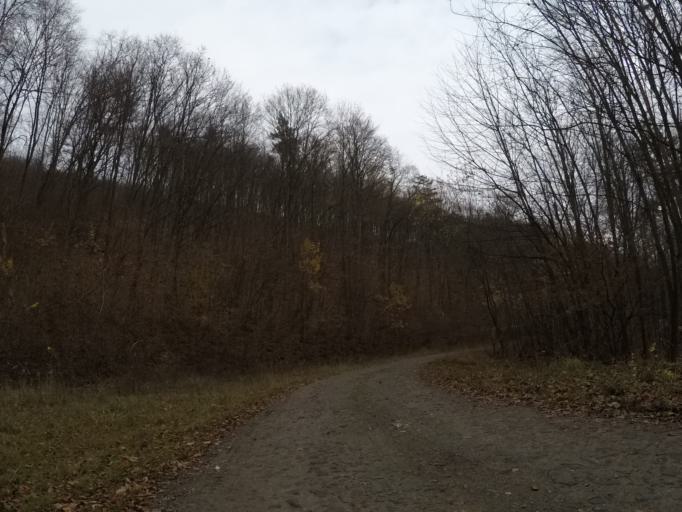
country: SK
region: Presovsky
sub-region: Okres Presov
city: Presov
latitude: 48.8920
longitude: 21.1965
